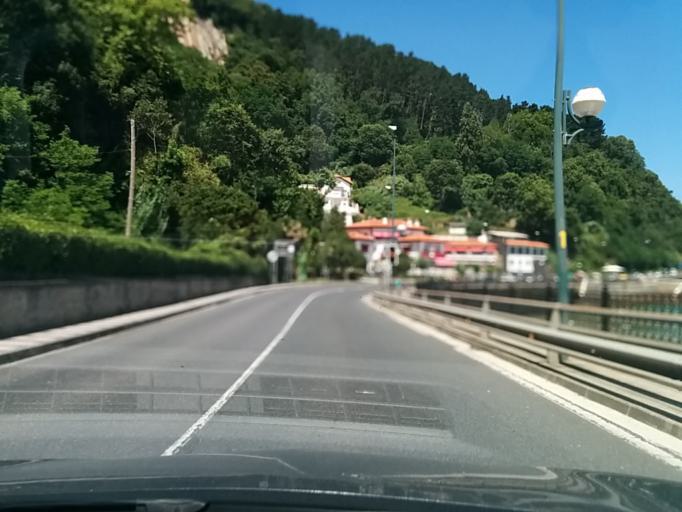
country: ES
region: Basque Country
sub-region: Provincia de Guipuzcoa
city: Zarautz
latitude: 43.2872
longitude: -2.1780
